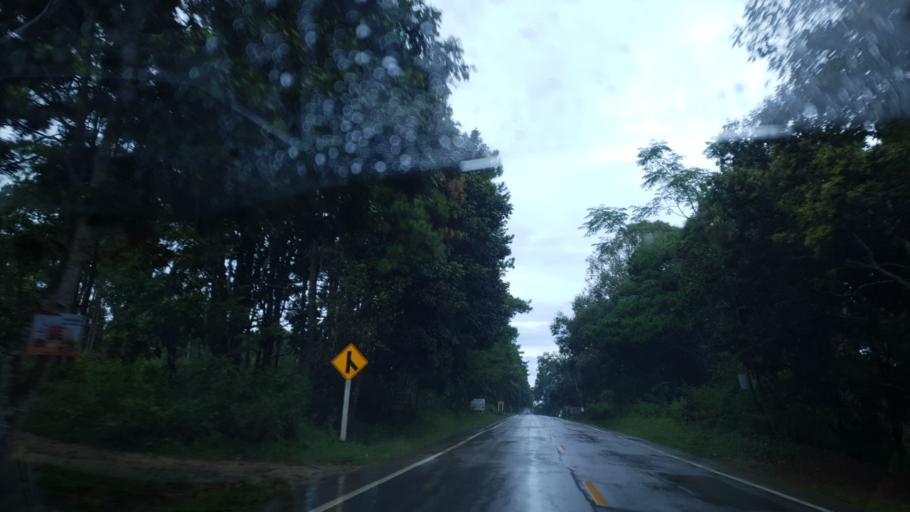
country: TH
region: Chiang Mai
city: Hot
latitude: 18.1432
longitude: 98.3398
